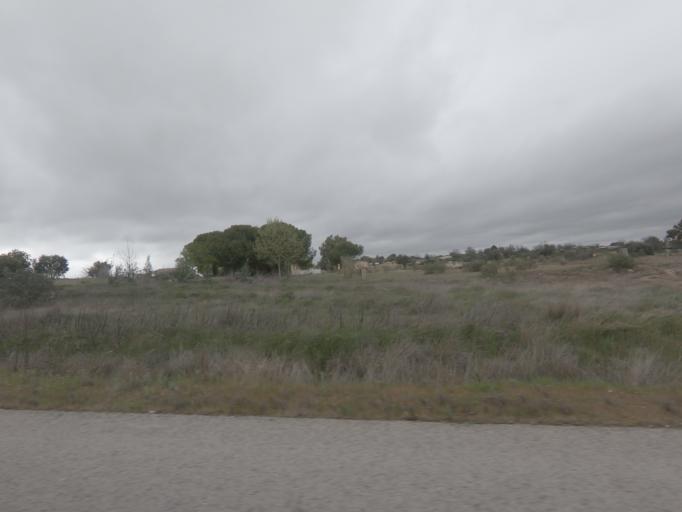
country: ES
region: Extremadura
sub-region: Provincia de Caceres
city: Malpartida de Caceres
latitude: 39.3831
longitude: -6.4427
